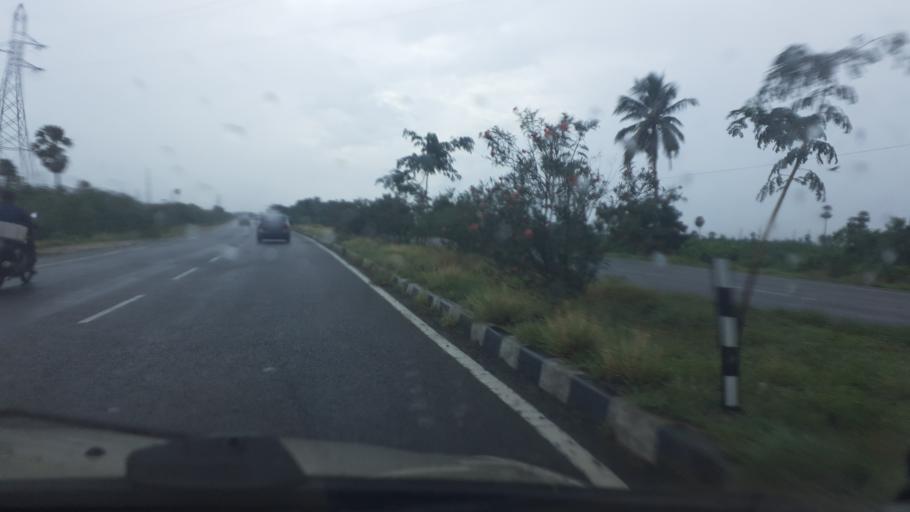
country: IN
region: Tamil Nadu
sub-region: Thoothukkudi
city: Kayattar
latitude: 8.9531
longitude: 77.7678
